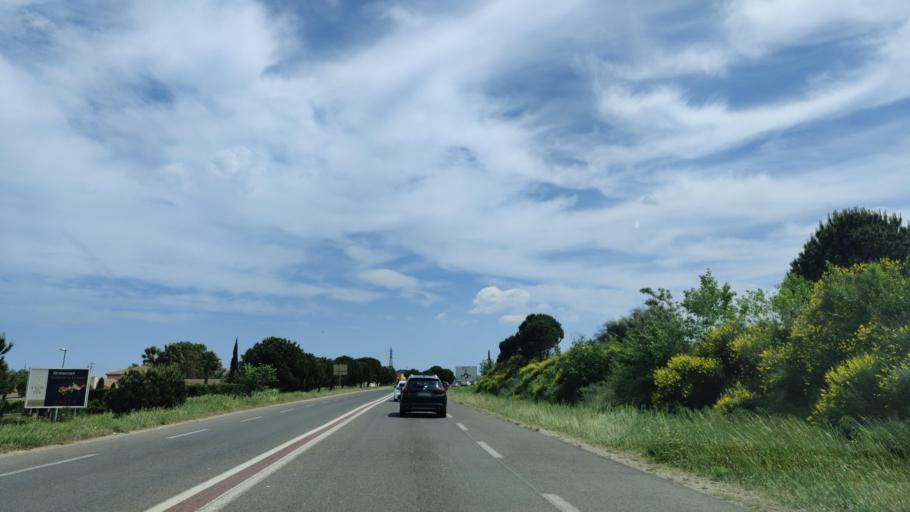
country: FR
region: Languedoc-Roussillon
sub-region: Departement des Pyrenees-Orientales
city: Perpignan
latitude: 42.6708
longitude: 2.8946
